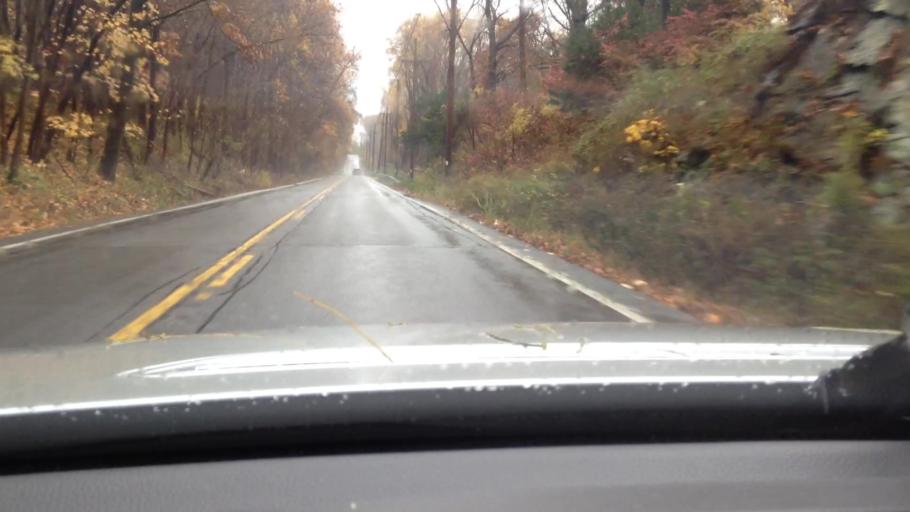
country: US
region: New York
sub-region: Orange County
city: Cornwall-on-Hudson
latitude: 41.4572
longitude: -73.9815
